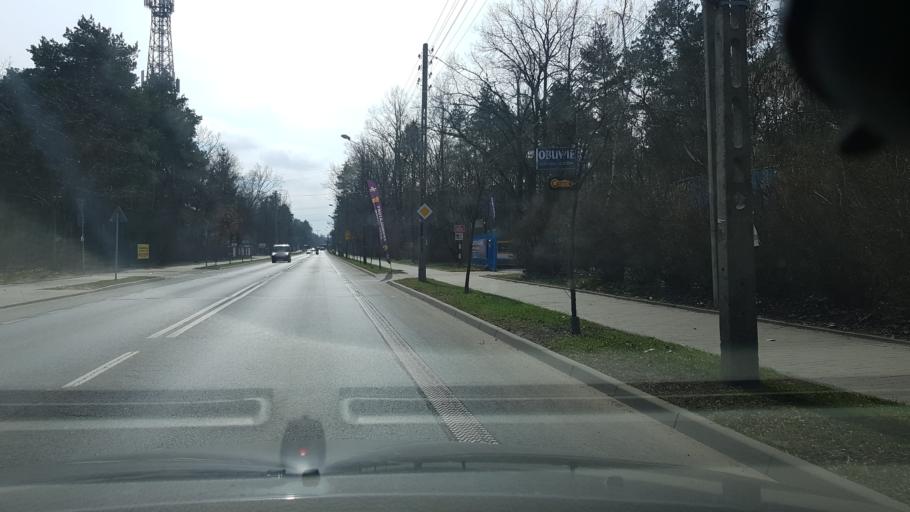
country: PL
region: Masovian Voivodeship
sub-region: Warszawa
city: Wesola
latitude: 52.2498
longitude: 21.2236
